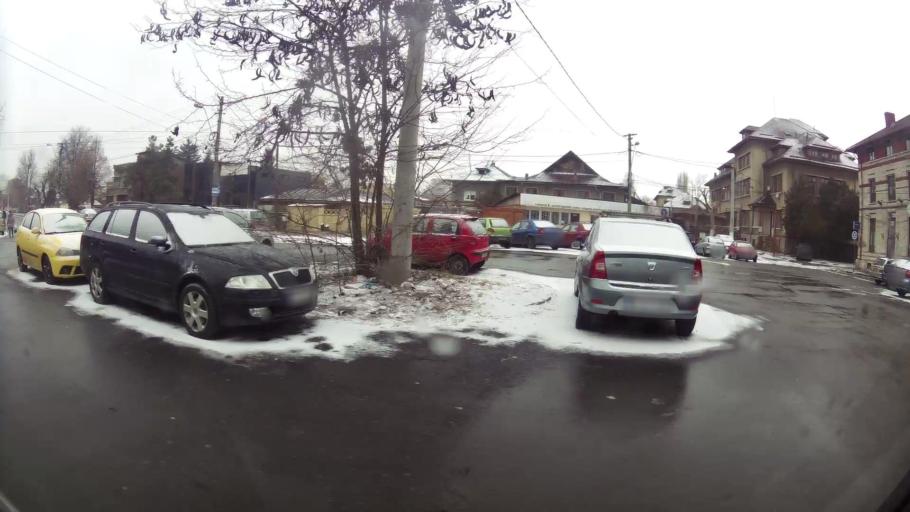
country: RO
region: Prahova
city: Ploiesti
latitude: 44.9533
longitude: 26.0268
